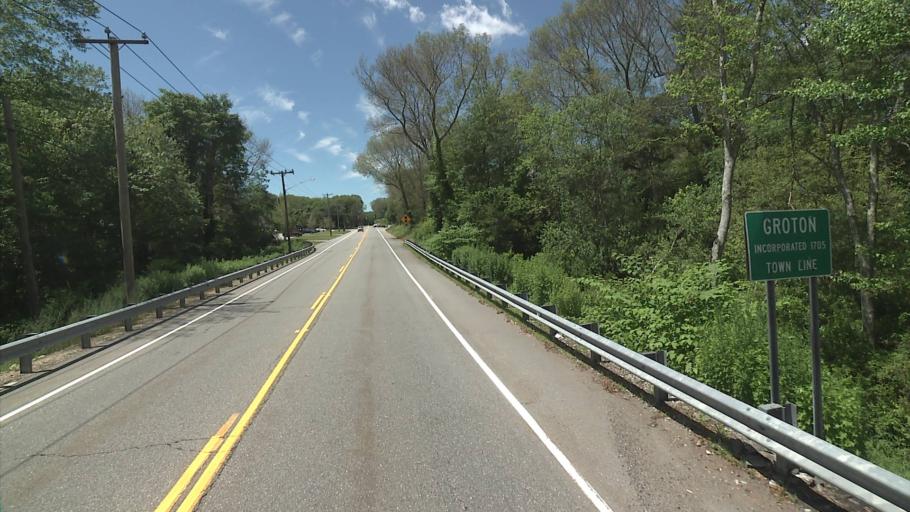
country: US
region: Connecticut
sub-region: New London County
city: Old Mystic
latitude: 41.3946
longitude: -71.9610
